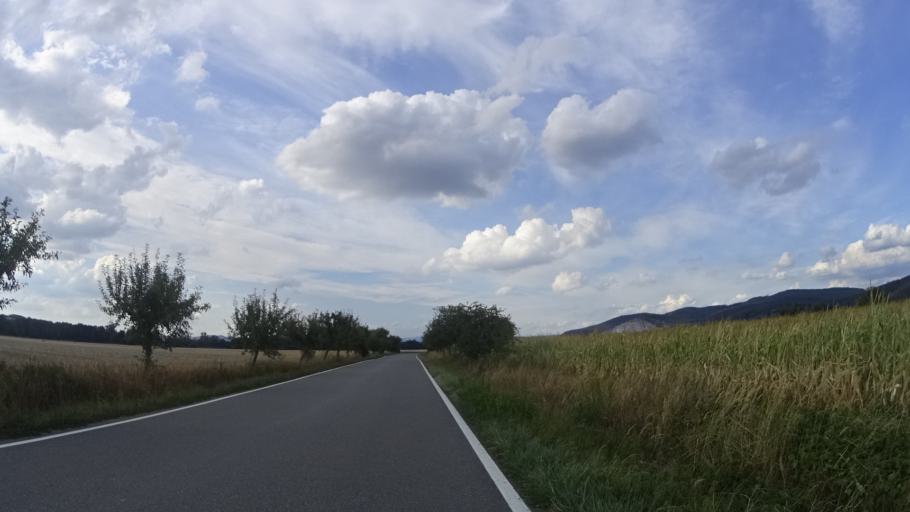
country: CZ
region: Olomoucky
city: Dubicko
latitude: 49.8285
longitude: 16.9358
